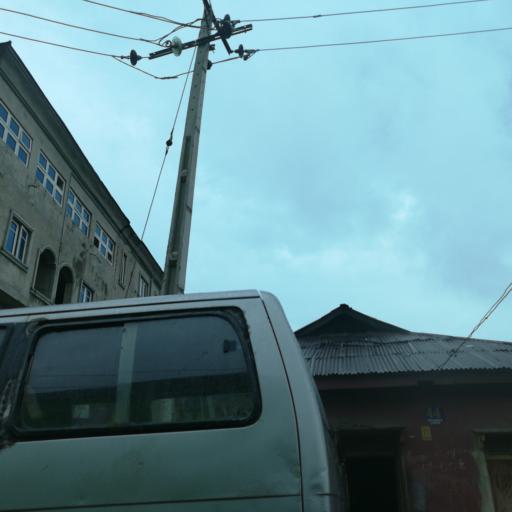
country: NG
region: Lagos
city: Oshodi
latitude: 6.5558
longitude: 3.3470
